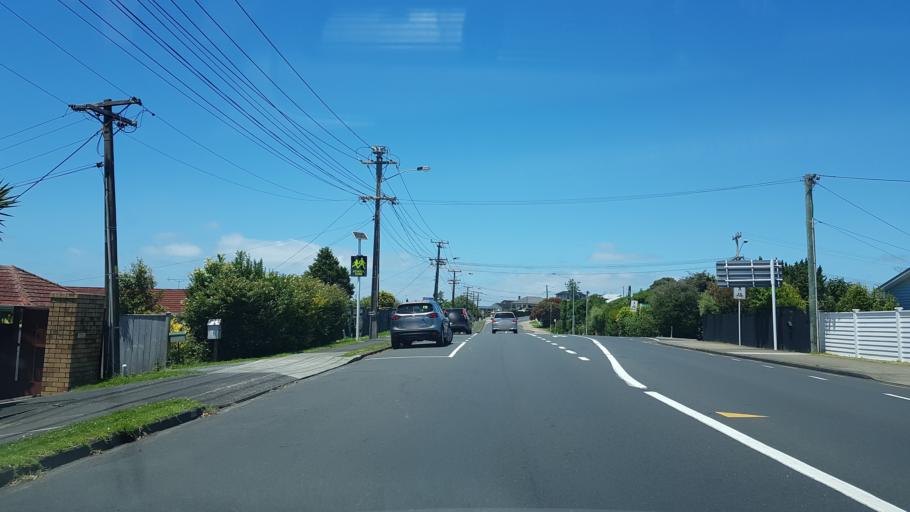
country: NZ
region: Auckland
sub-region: Auckland
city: North Shore
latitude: -36.7705
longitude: 174.7495
